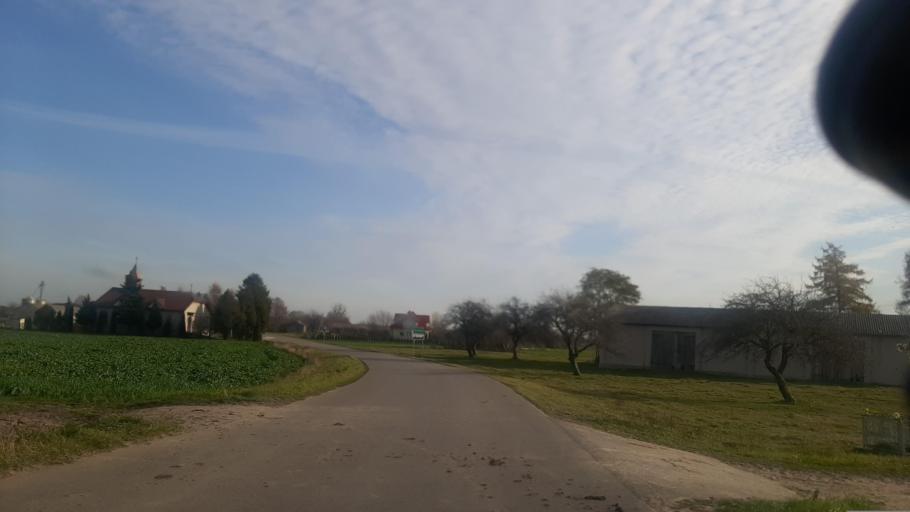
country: PL
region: Lublin Voivodeship
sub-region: Powiat lubelski
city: Garbow
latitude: 51.3851
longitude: 22.3718
